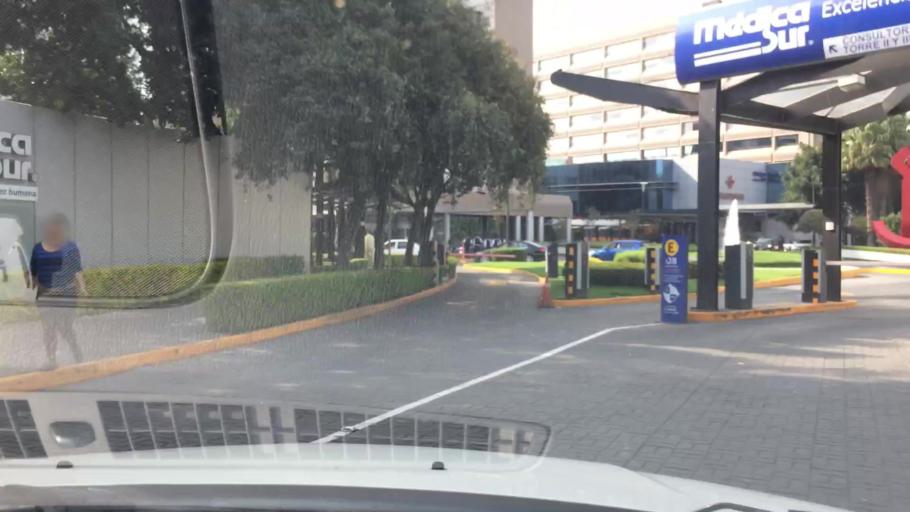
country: MX
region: Mexico City
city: Tlalpan
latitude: 19.2966
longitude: -99.1607
